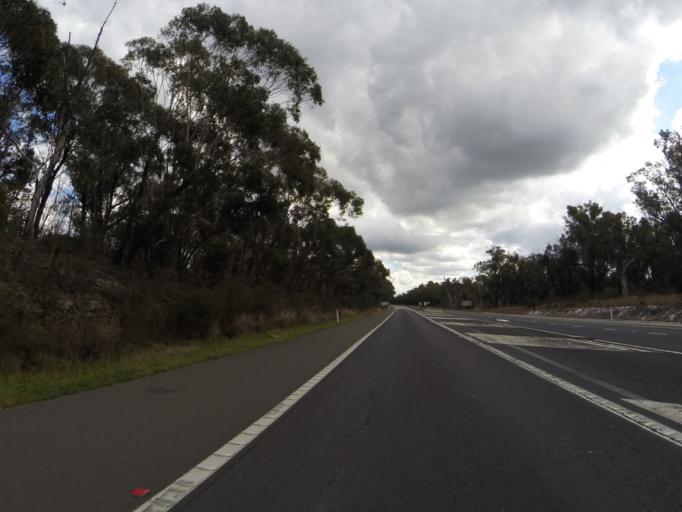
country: AU
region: New South Wales
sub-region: Wollongong
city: Mount Keira
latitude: -34.3277
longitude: 150.7751
